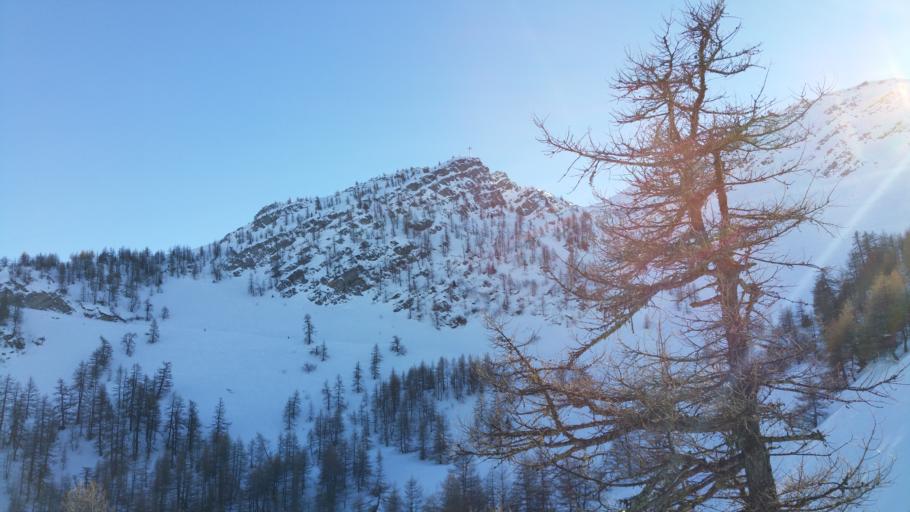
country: FR
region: Rhone-Alpes
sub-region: Departement de la Savoie
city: Villargondran
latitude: 45.2167
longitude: 6.3964
